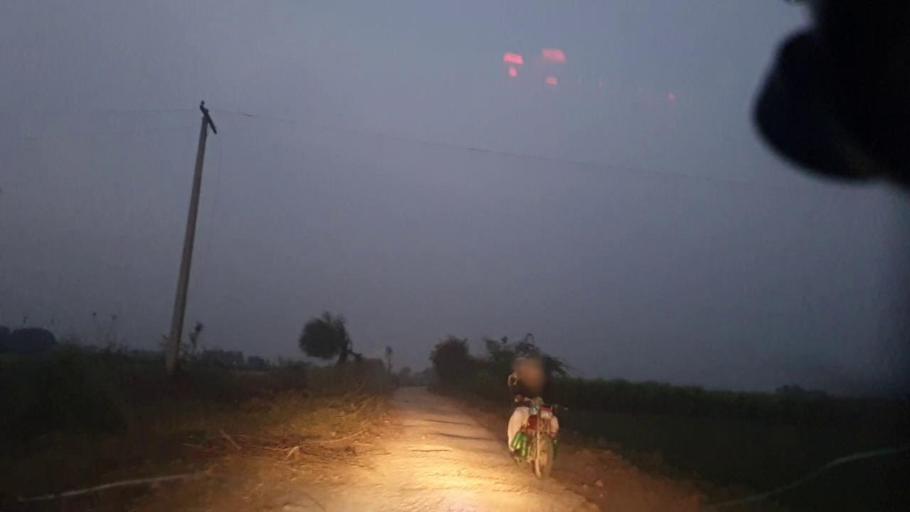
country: PK
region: Sindh
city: Hingorja
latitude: 27.2085
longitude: 68.3715
